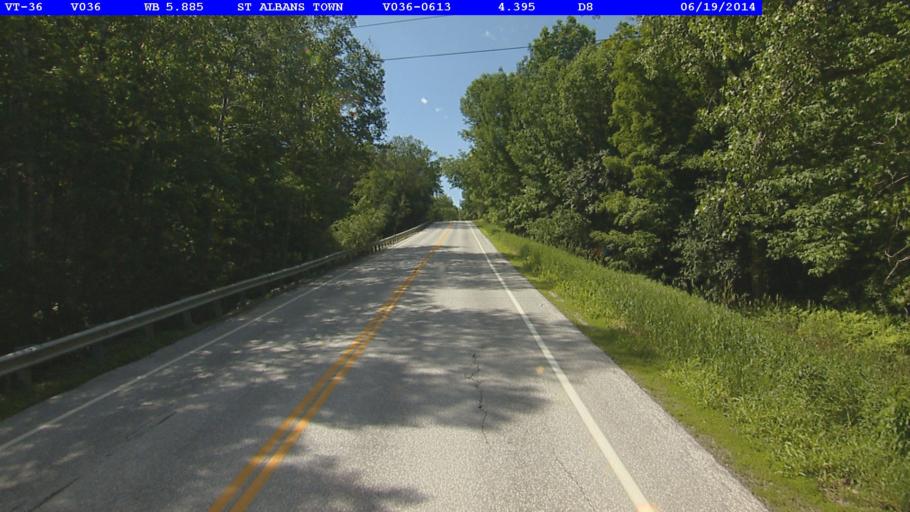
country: US
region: Vermont
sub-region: Franklin County
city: Saint Albans
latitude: 44.7939
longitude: -73.0470
